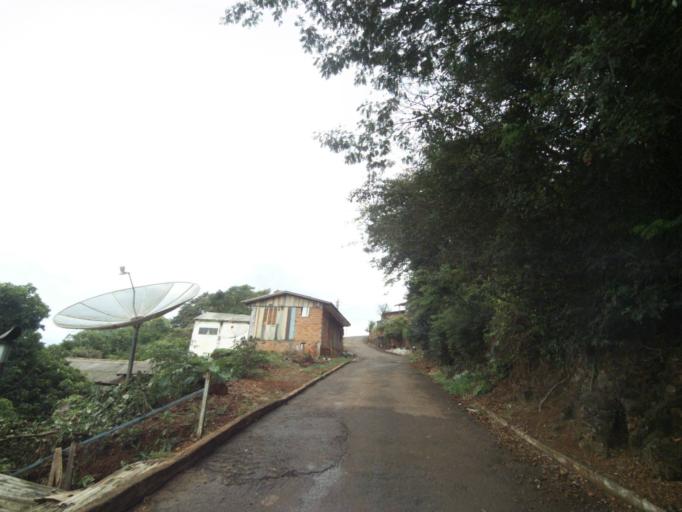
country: BR
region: Parana
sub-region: Guaraniacu
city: Guaraniacu
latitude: -25.0947
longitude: -52.8724
